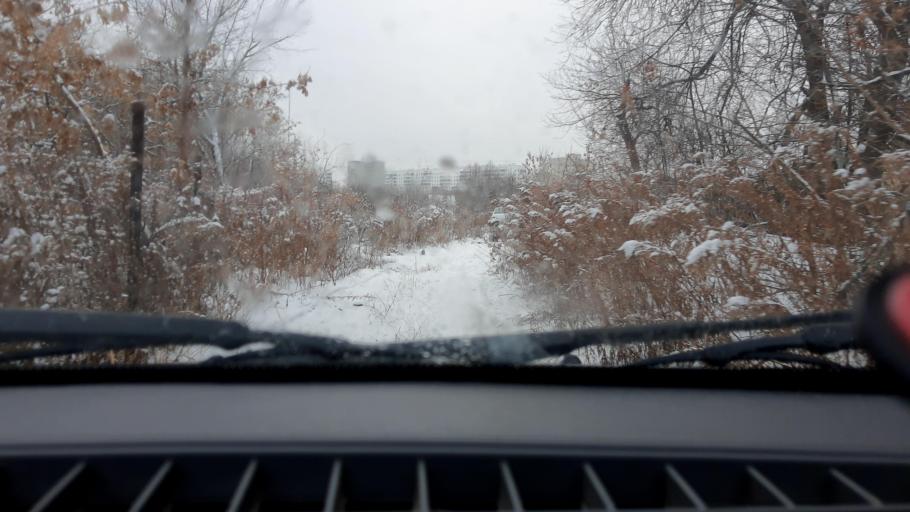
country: RU
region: Bashkortostan
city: Ufa
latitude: 54.8262
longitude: 56.1291
